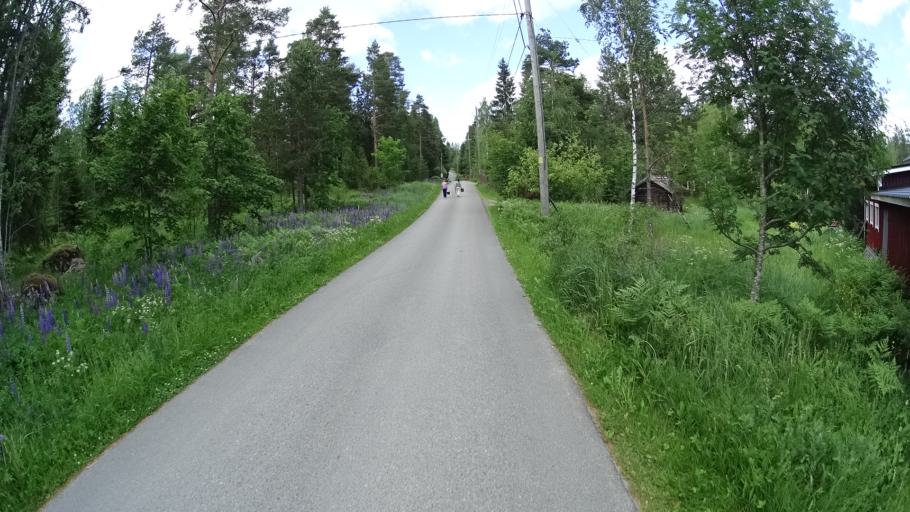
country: FI
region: Uusimaa
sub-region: Helsinki
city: Sibbo
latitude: 60.2602
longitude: 25.3210
